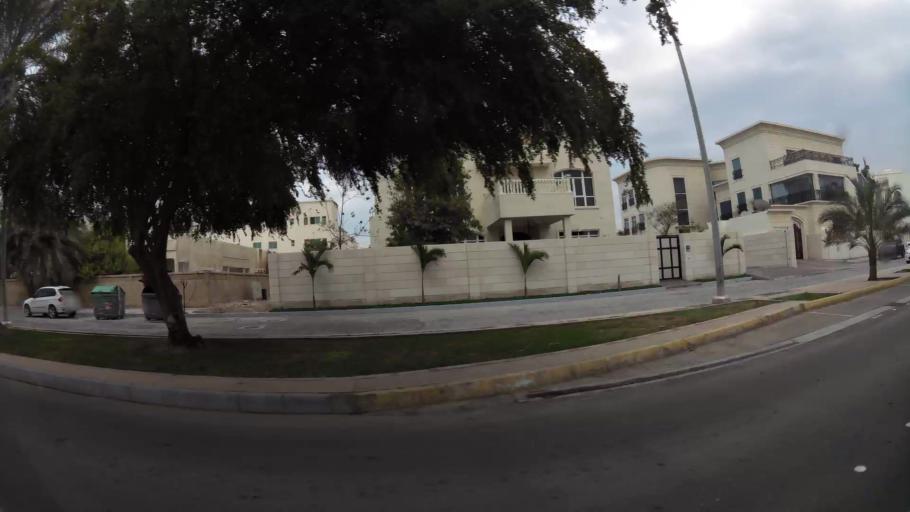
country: AE
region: Abu Dhabi
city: Abu Dhabi
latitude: 24.4506
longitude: 54.3519
